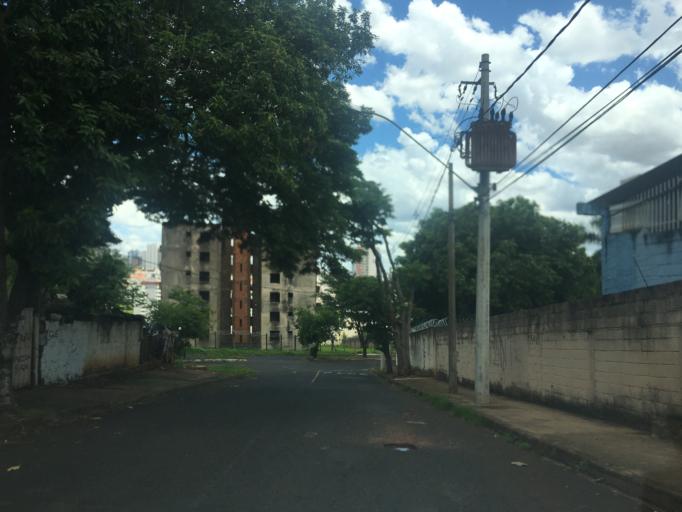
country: BR
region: Minas Gerais
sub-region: Uberlandia
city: Uberlandia
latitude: -18.9314
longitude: -48.3000
